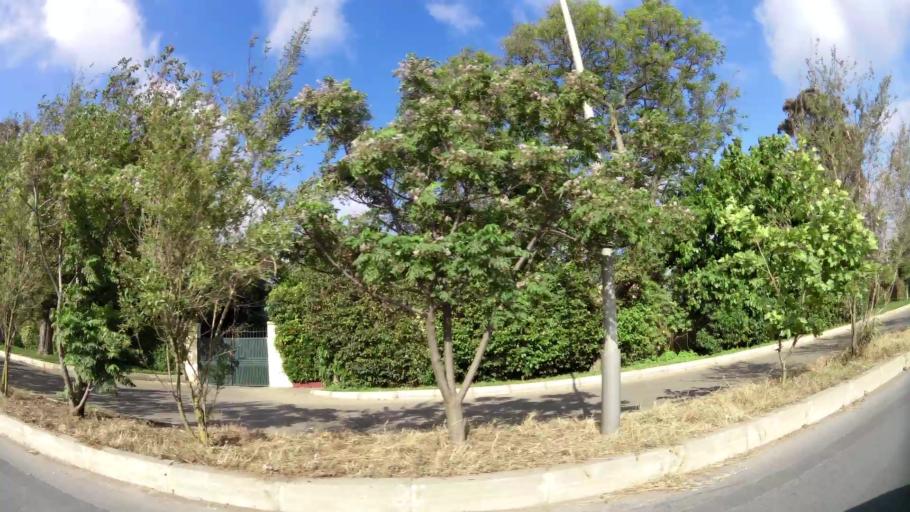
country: MA
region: Rabat-Sale-Zemmour-Zaer
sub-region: Rabat
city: Rabat
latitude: 33.9570
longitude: -6.8504
